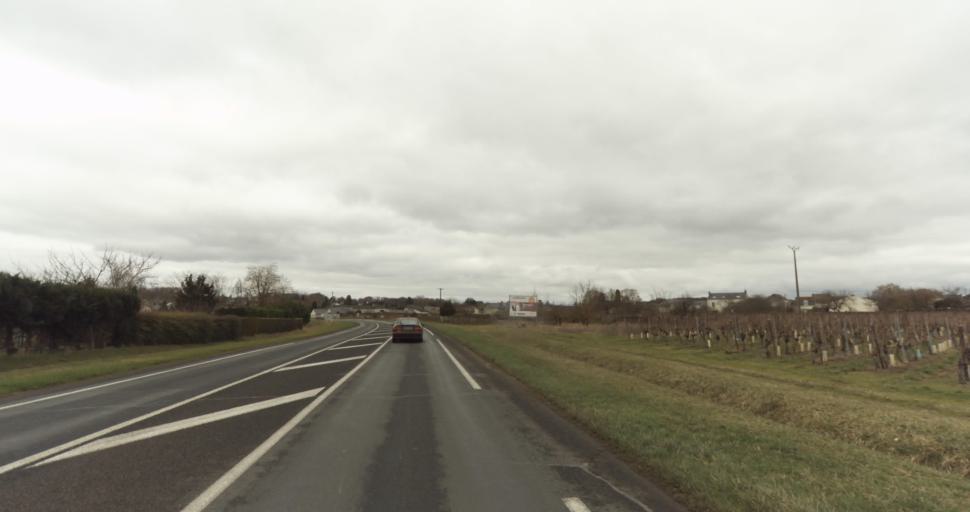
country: FR
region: Pays de la Loire
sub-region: Departement de Maine-et-Loire
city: Varrains
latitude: 47.2194
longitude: -0.0597
